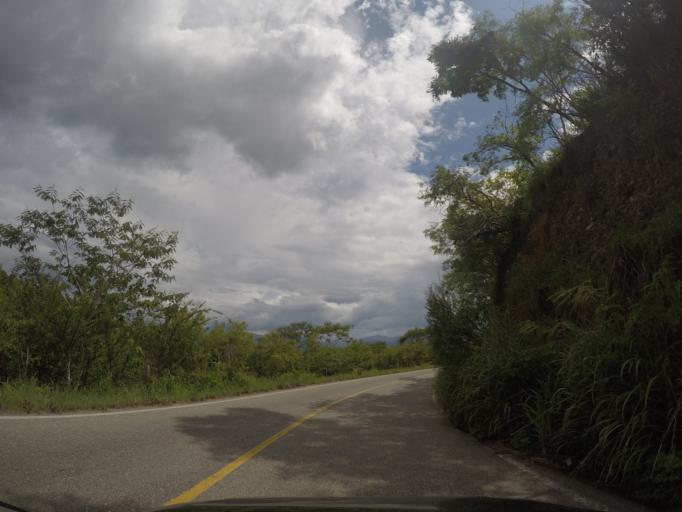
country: MX
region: Oaxaca
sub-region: San Jeronimo Coatlan
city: San Cristobal Honduras
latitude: 16.4352
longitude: -97.0568
